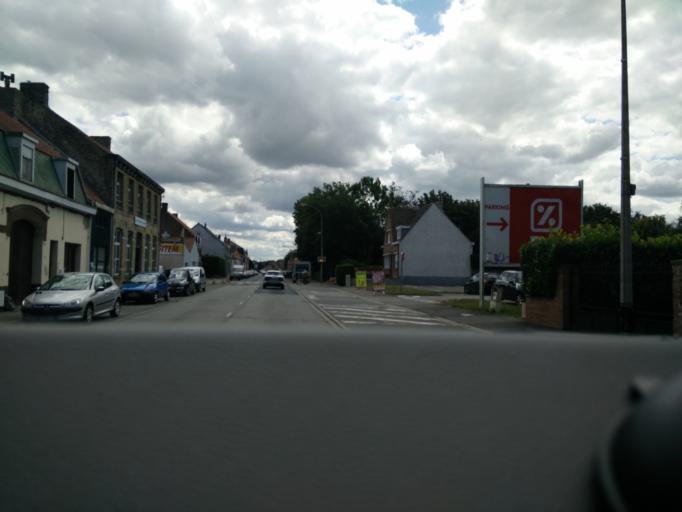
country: FR
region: Nord-Pas-de-Calais
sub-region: Departement du Nord
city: Bergues
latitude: 50.9607
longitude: 2.4333
